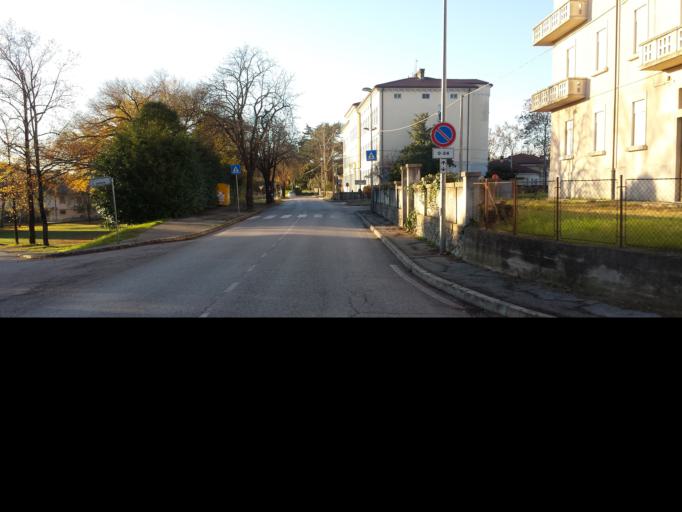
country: IT
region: Friuli Venezia Giulia
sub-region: Provincia di Gorizia
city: Gradisca d'Isonzo
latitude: 45.8938
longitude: 13.4958
